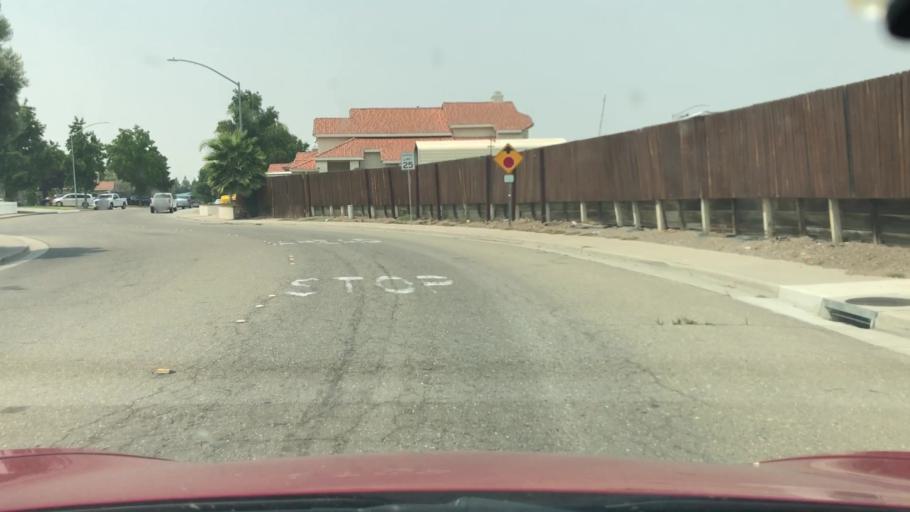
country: US
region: California
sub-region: San Joaquin County
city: Tracy
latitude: 37.7390
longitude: -121.4440
